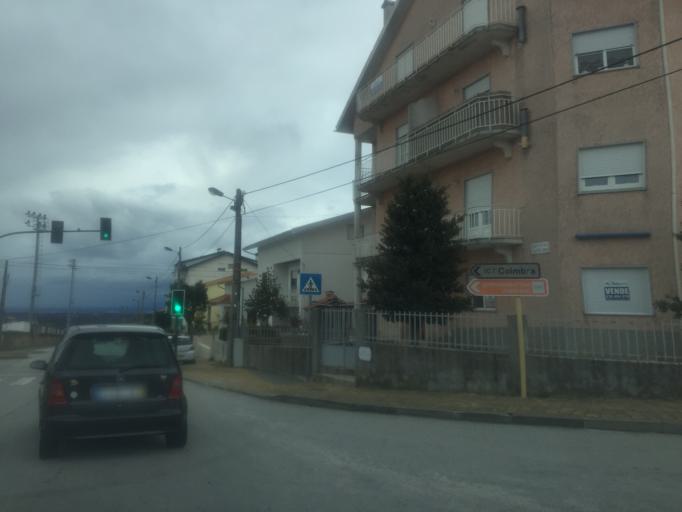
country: PT
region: Guarda
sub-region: Seia
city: Seia
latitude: 40.4037
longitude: -7.7169
